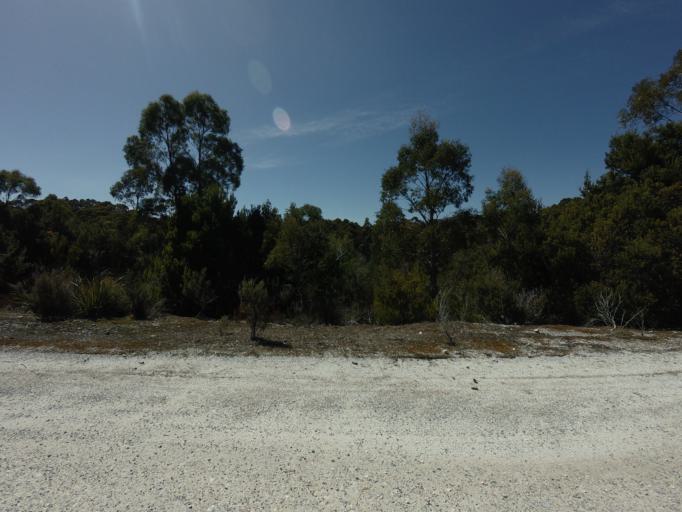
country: AU
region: Tasmania
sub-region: Huon Valley
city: Geeveston
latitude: -43.0366
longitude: 146.2969
